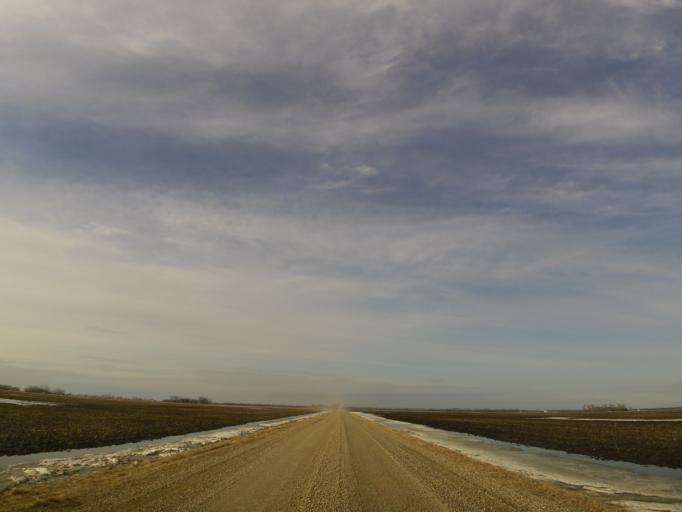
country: US
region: North Dakota
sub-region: Walsh County
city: Grafton
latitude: 48.4136
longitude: -97.2121
